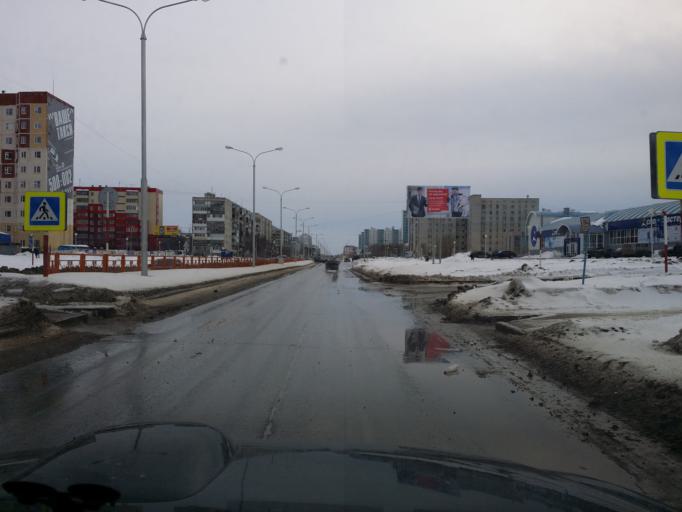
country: RU
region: Khanty-Mansiyskiy Avtonomnyy Okrug
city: Nizhnevartovsk
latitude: 60.9467
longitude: 76.6033
